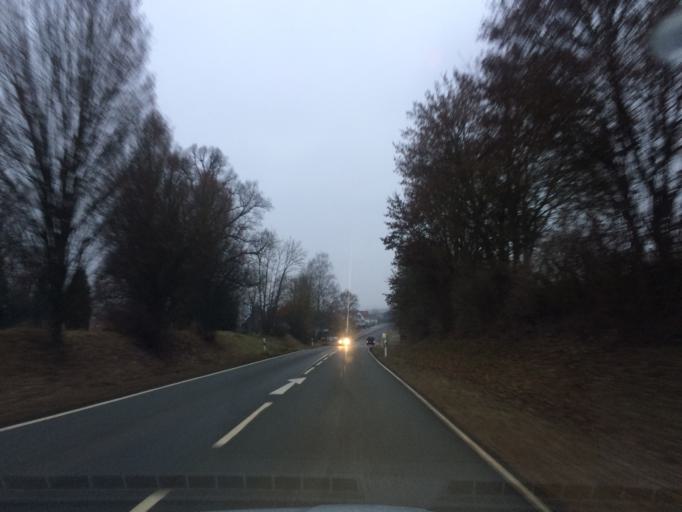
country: DE
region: Hesse
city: Trendelburg
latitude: 51.5561
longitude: 9.3828
